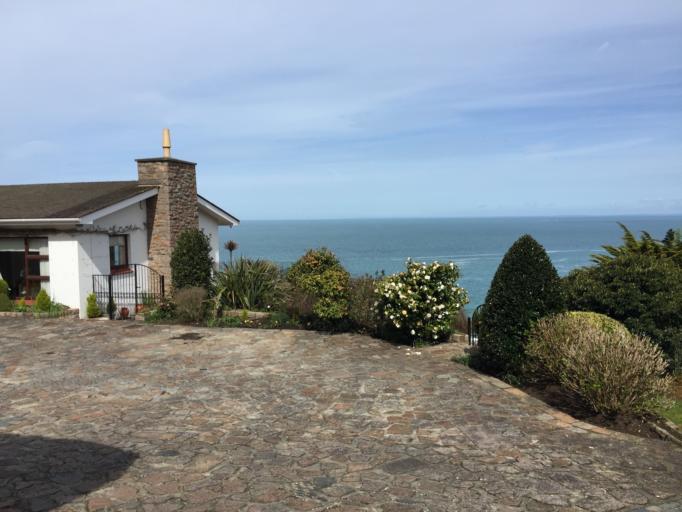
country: JE
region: St Helier
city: Saint Helier
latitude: 49.2466
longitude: -2.2026
